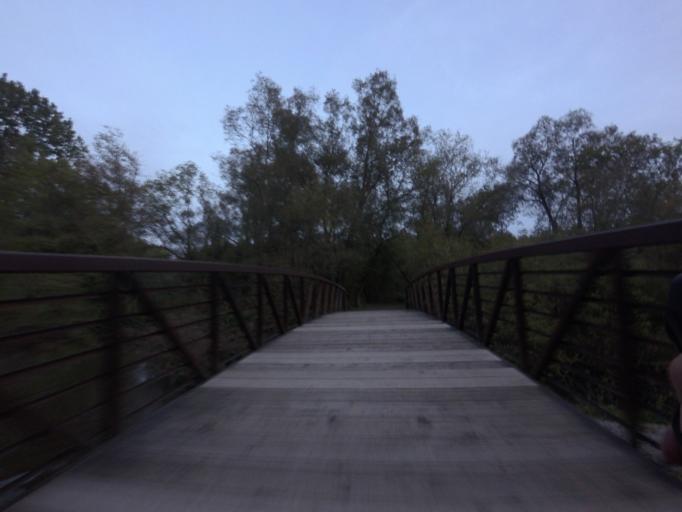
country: CA
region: Ontario
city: Oshawa
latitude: 43.9022
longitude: -78.6010
